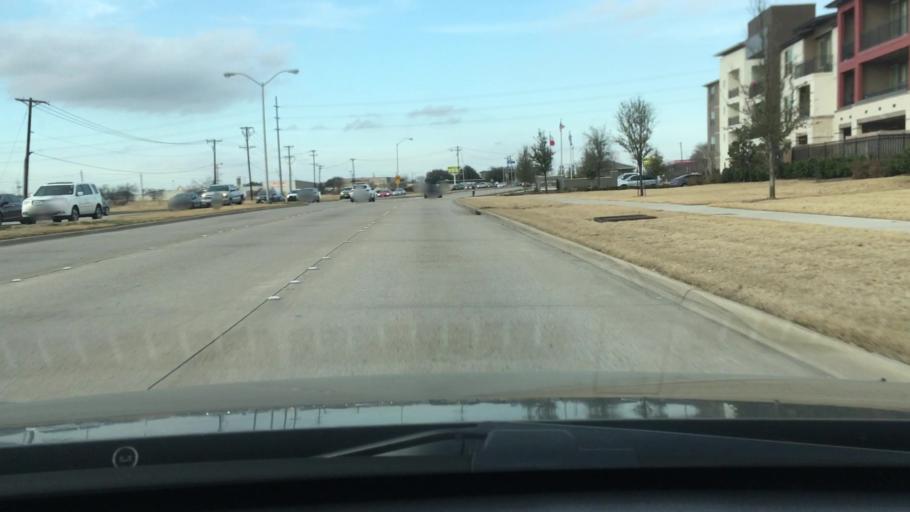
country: US
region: Texas
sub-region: Dallas County
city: Richardson
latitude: 33.0052
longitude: -96.7676
